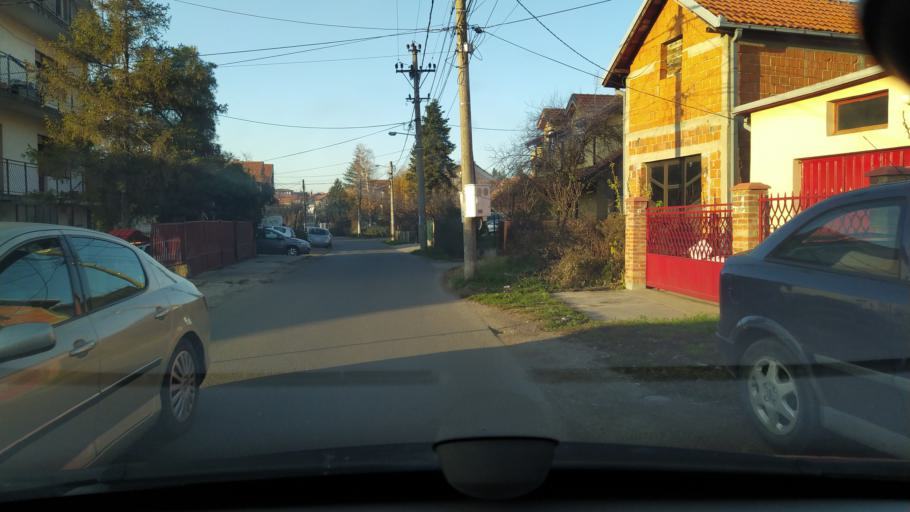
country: RS
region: Central Serbia
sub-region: Belgrade
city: Zvezdara
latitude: 44.7611
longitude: 20.5641
